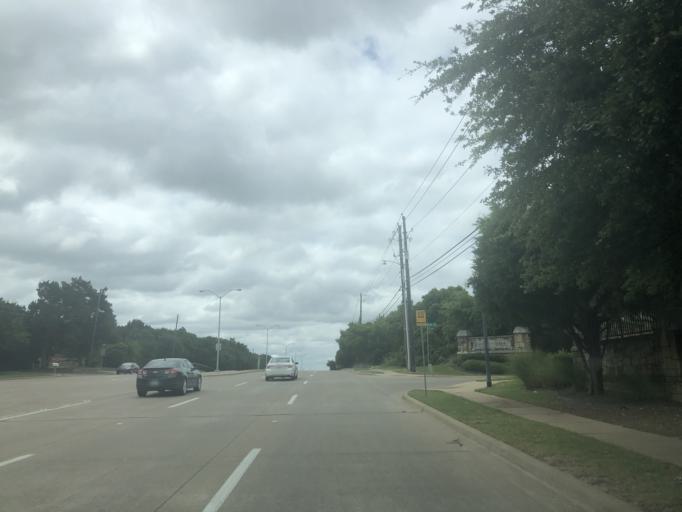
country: US
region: Texas
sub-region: Dallas County
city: Duncanville
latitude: 32.6597
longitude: -96.9433
